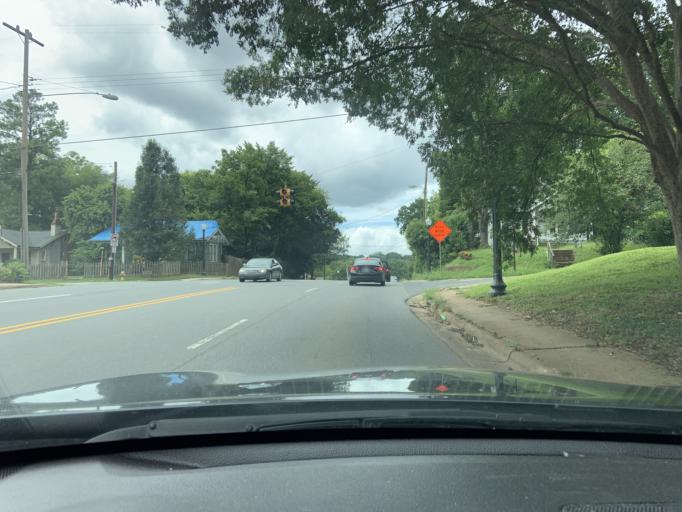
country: US
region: North Carolina
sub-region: Mecklenburg County
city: Charlotte
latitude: 35.2165
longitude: -80.8686
